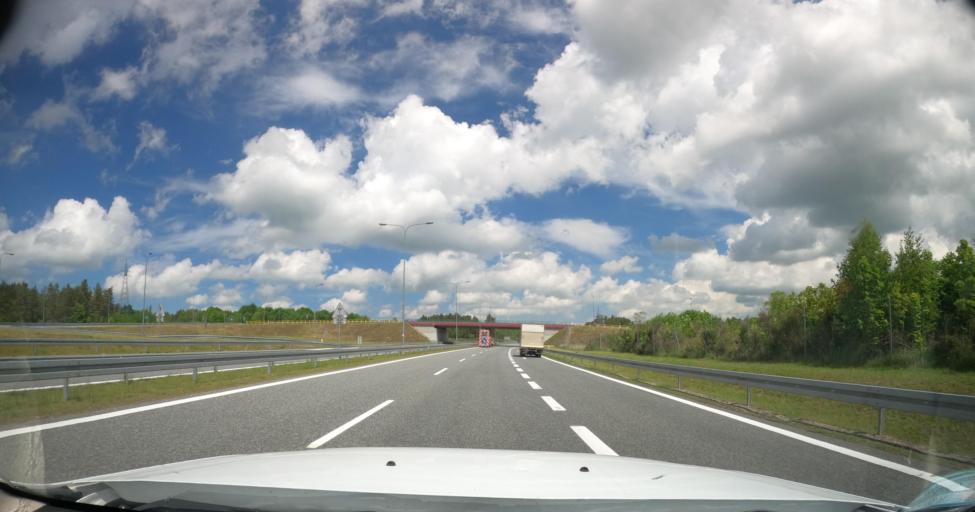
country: PL
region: Pomeranian Voivodeship
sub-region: Slupsk
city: Slupsk
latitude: 54.4498
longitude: 17.0813
